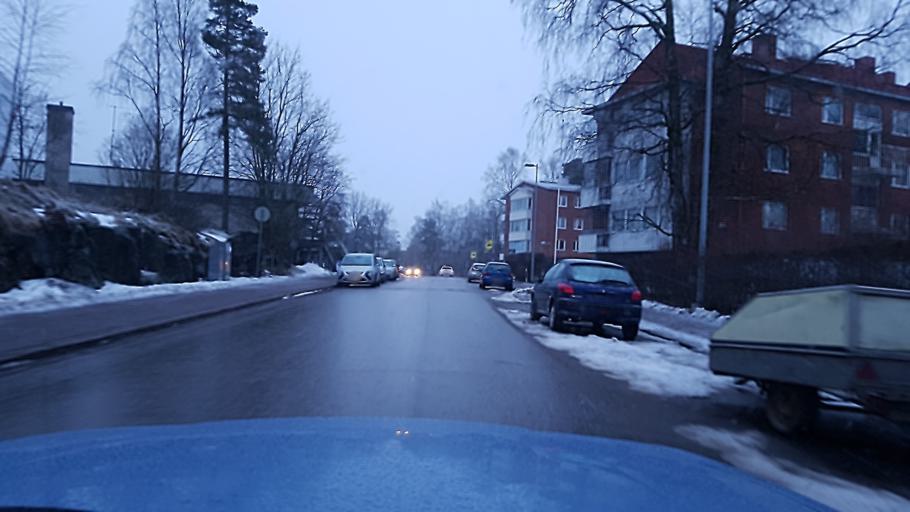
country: FI
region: Uusimaa
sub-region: Helsinki
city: Helsinki
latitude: 60.1873
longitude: 25.0077
